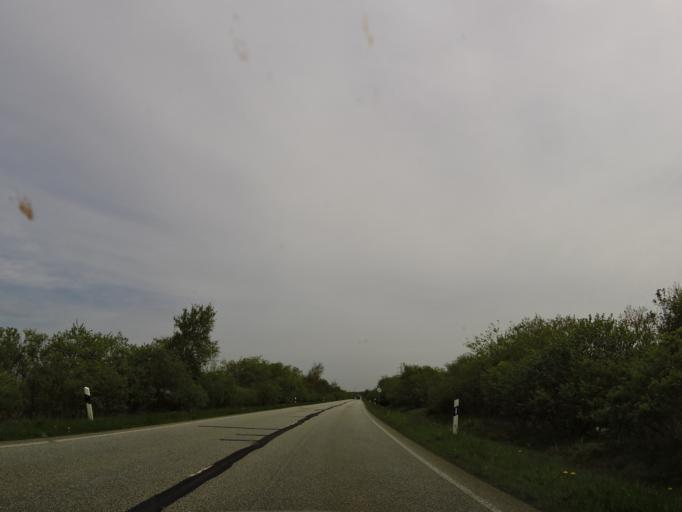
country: DE
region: Schleswig-Holstein
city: Husum
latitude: 54.4555
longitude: 9.0490
